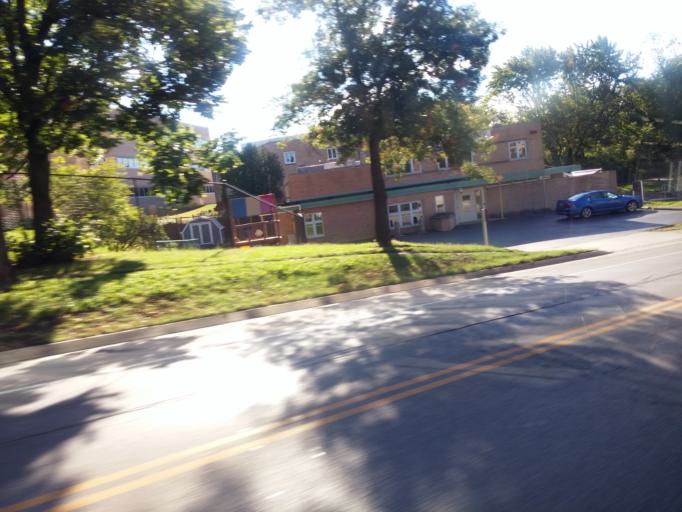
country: US
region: Wisconsin
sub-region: Dane County
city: Shorewood Hills
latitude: 43.0750
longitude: -89.4339
